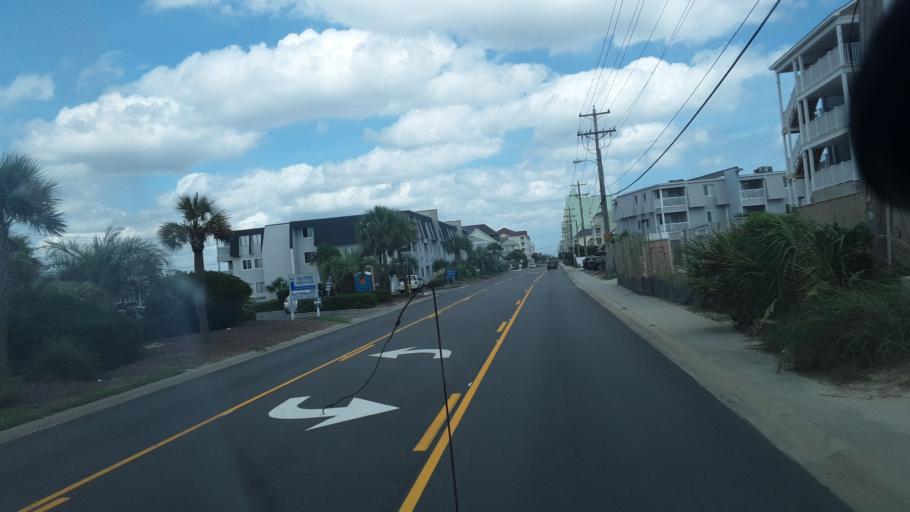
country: US
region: South Carolina
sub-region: Horry County
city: Little River
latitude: 33.8357
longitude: -78.6189
